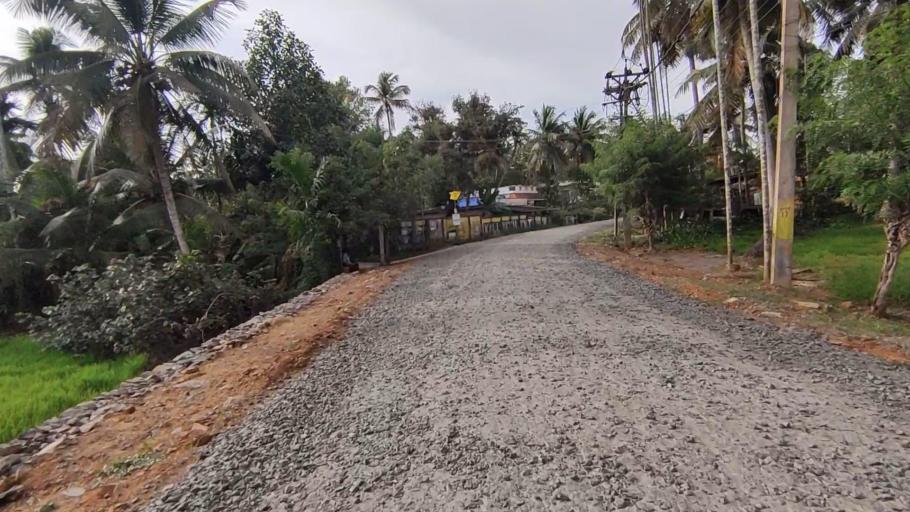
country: IN
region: Kerala
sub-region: Kottayam
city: Kottayam
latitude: 9.5788
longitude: 76.4918
